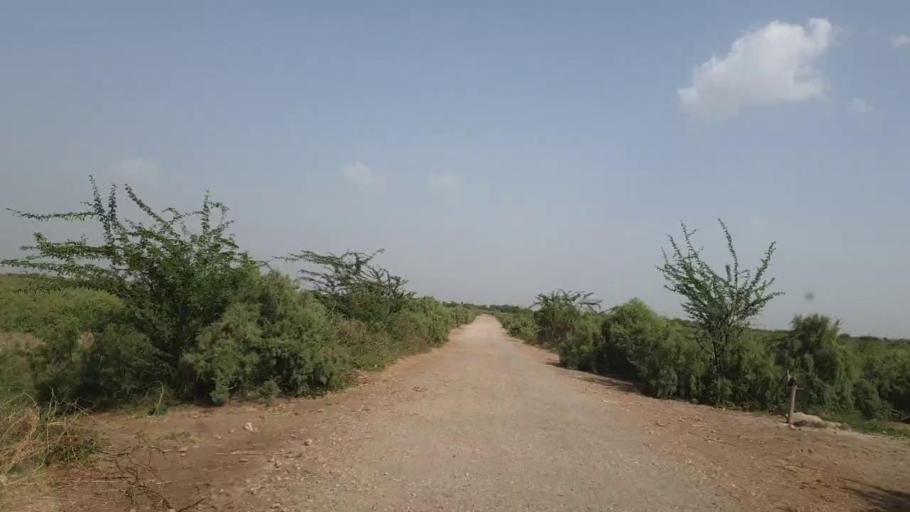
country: PK
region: Sindh
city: Rajo Khanani
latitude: 25.0326
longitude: 68.8757
